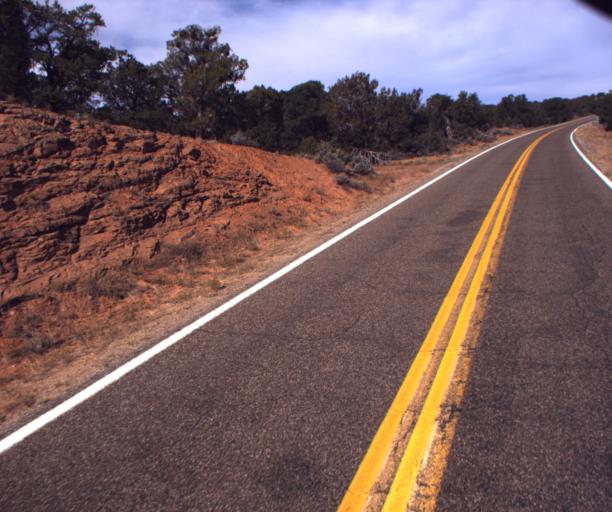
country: US
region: Arizona
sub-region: Navajo County
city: Kayenta
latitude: 36.6202
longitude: -110.5073
